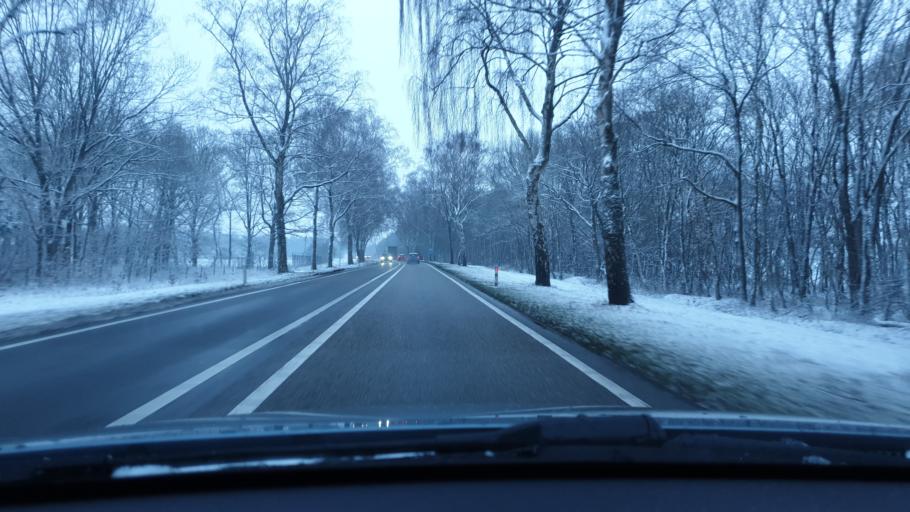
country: NL
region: North Brabant
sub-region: Gemeente Landerd
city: Reek
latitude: 51.7305
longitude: 5.6690
